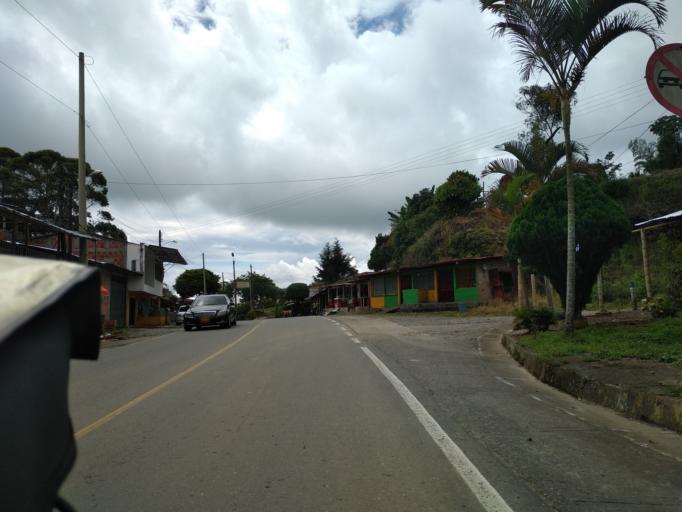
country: CO
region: Valle del Cauca
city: Sevilla
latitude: 4.2693
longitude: -75.9174
